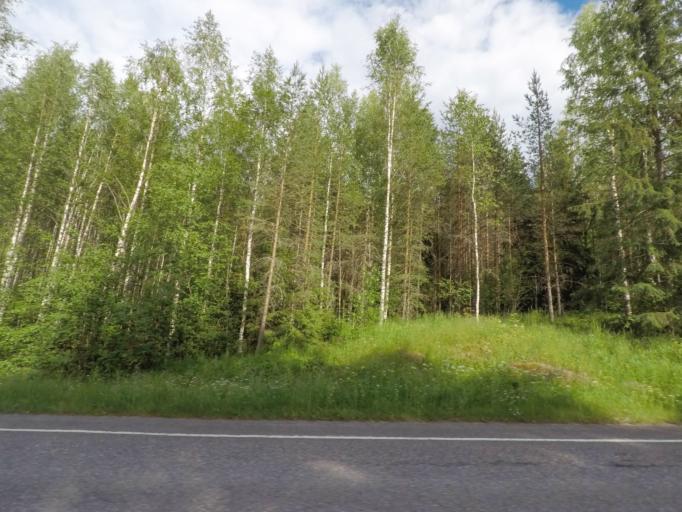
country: FI
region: Paijanne Tavastia
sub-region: Lahti
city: Hollola
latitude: 60.8178
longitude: 25.4840
